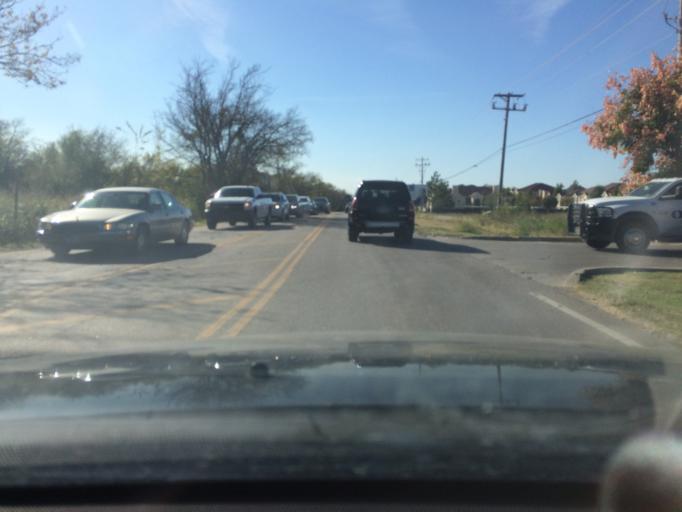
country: US
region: Oklahoma
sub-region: Tulsa County
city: Broken Arrow
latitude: 36.0900
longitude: -95.8158
